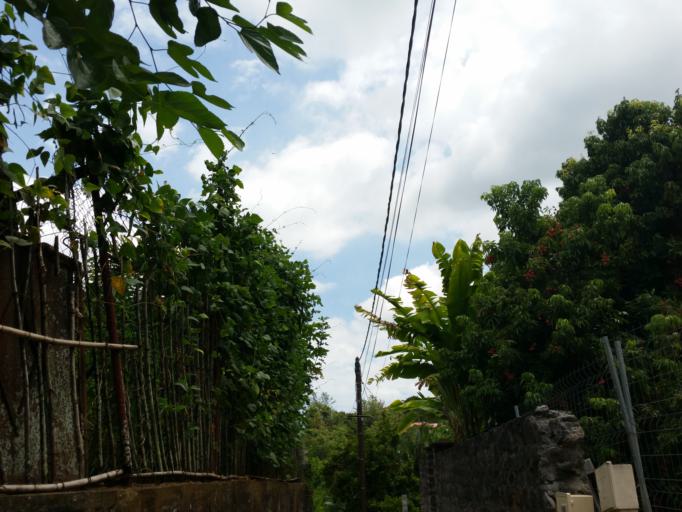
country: RE
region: Reunion
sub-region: Reunion
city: L'Entre-Deux
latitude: -21.2505
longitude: 55.4671
